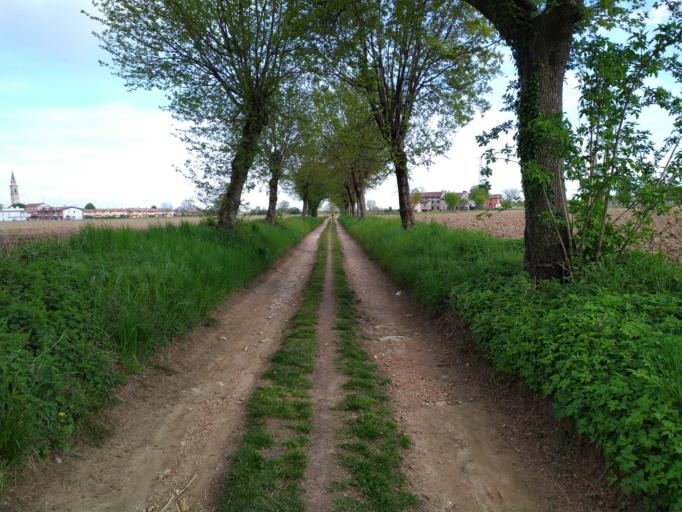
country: IT
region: Veneto
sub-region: Provincia di Vicenza
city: Giavenale
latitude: 45.6971
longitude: 11.3953
